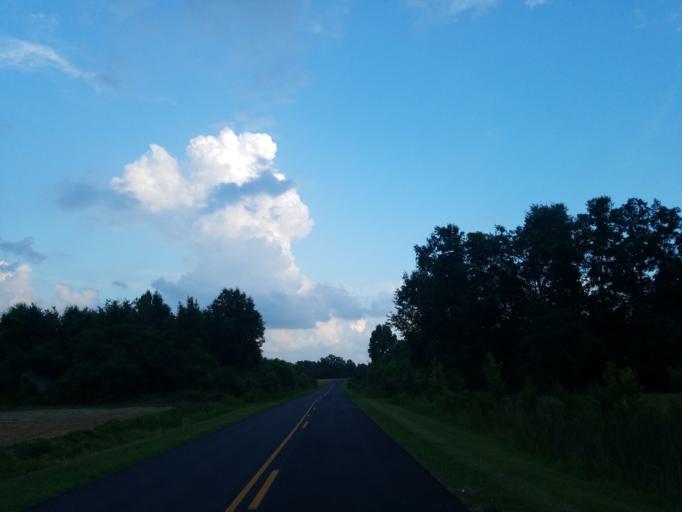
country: US
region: Georgia
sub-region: Dooly County
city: Unadilla
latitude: 32.1889
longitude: -83.7566
